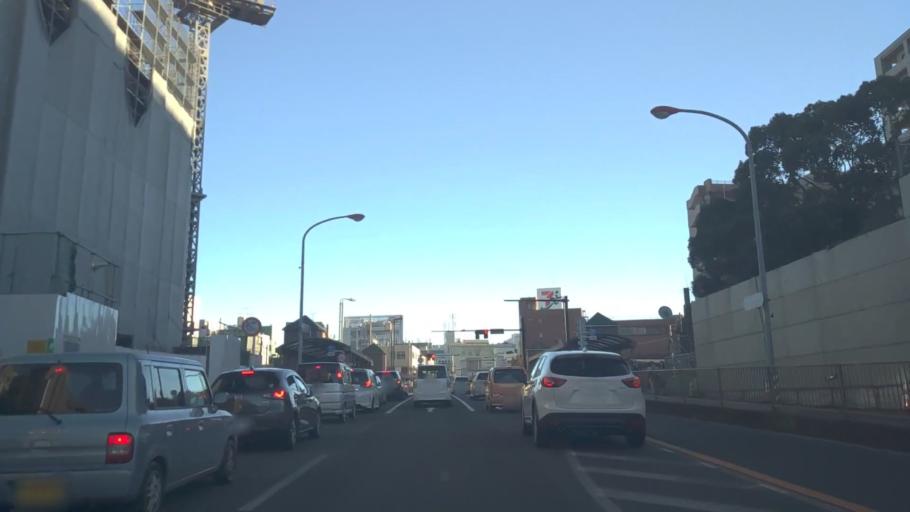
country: JP
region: Kanagawa
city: Chigasaki
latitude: 35.3340
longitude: 139.4054
